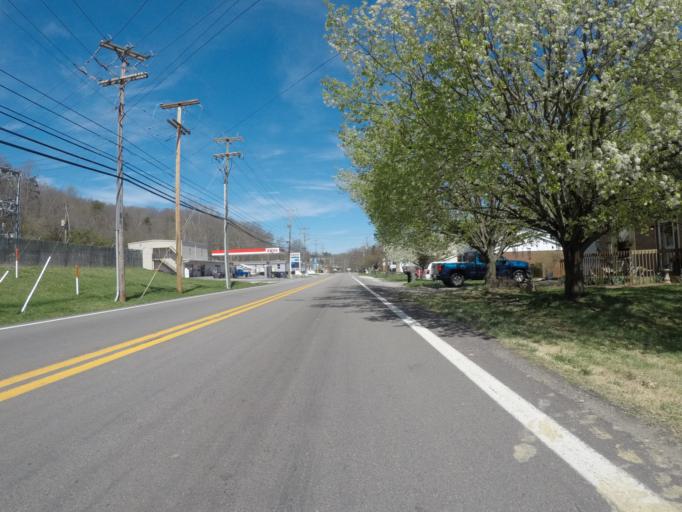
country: US
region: West Virginia
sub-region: Cabell County
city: Pea Ridge
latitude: 38.4027
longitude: -82.3199
